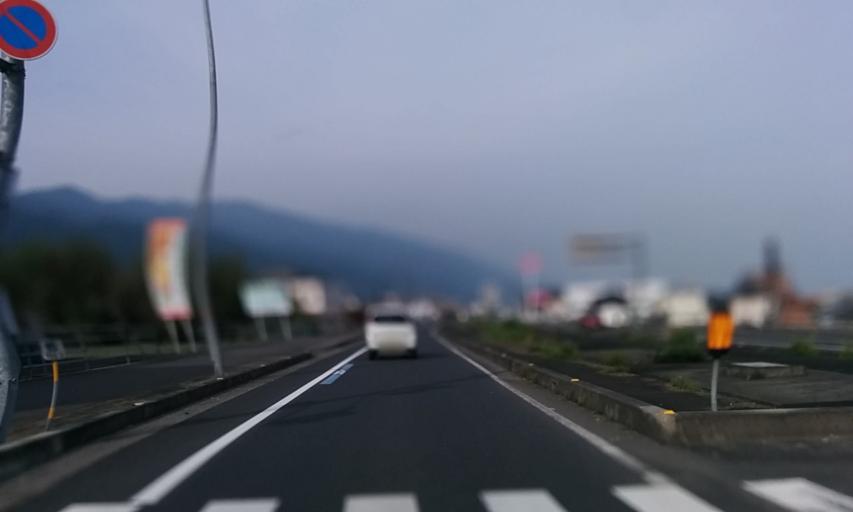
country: JP
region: Ehime
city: Kawanoecho
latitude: 33.9745
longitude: 133.5426
